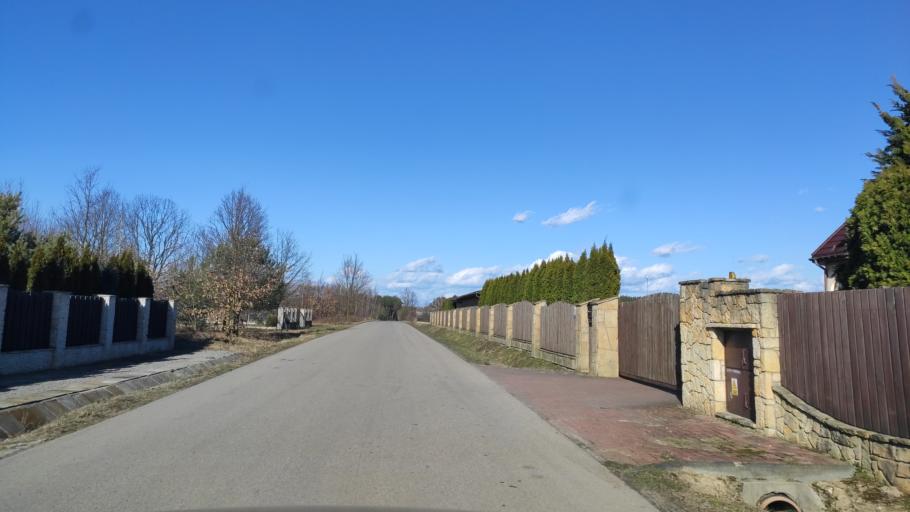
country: PL
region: Masovian Voivodeship
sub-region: Powiat radomski
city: Jastrzebia
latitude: 51.4553
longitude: 21.2580
